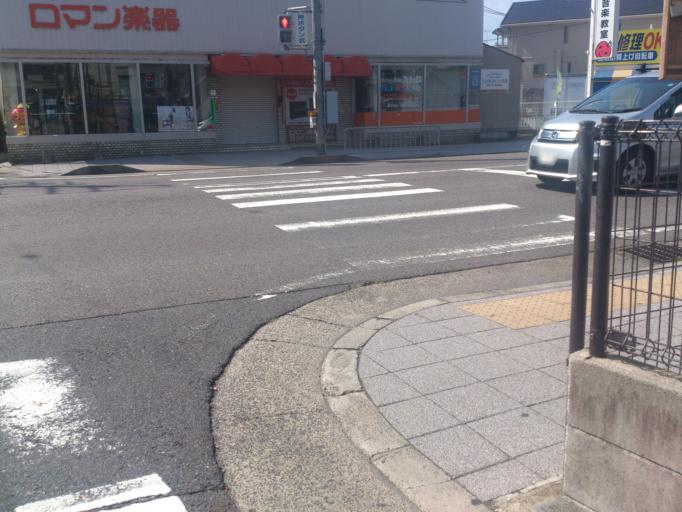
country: JP
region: Shiga Prefecture
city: Kusatsu
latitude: 34.9861
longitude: 135.9278
